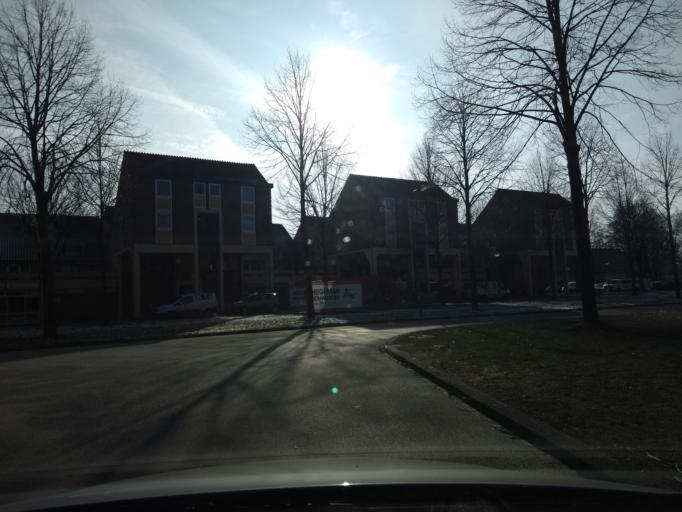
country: NL
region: Overijssel
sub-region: Gemeente Hengelo
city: Hengelo
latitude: 52.2670
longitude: 6.8305
